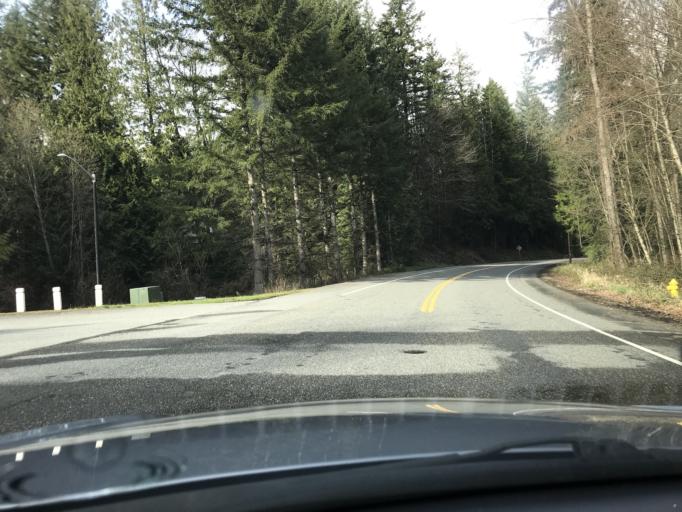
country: US
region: Washington
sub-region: King County
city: Ames Lake
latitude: 47.6354
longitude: -121.9714
